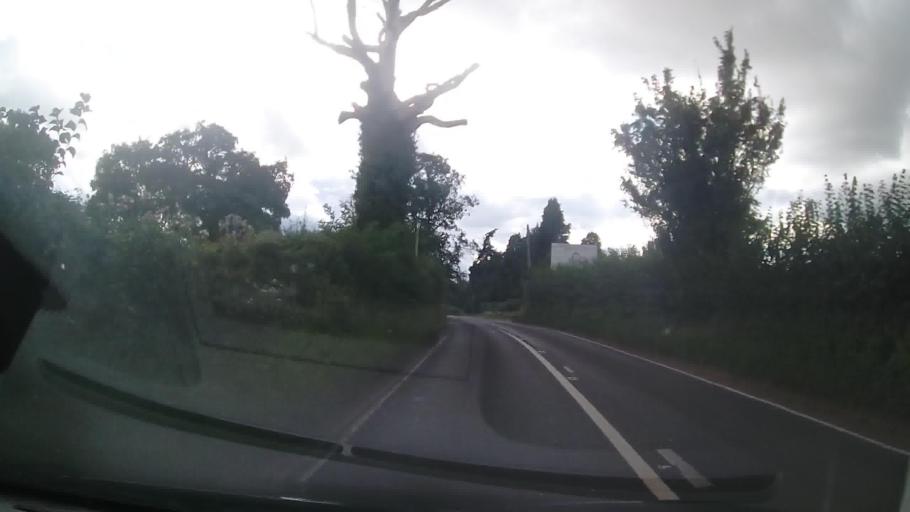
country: GB
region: England
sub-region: Shropshire
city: Great Hanwood
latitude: 52.6917
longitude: -2.8002
